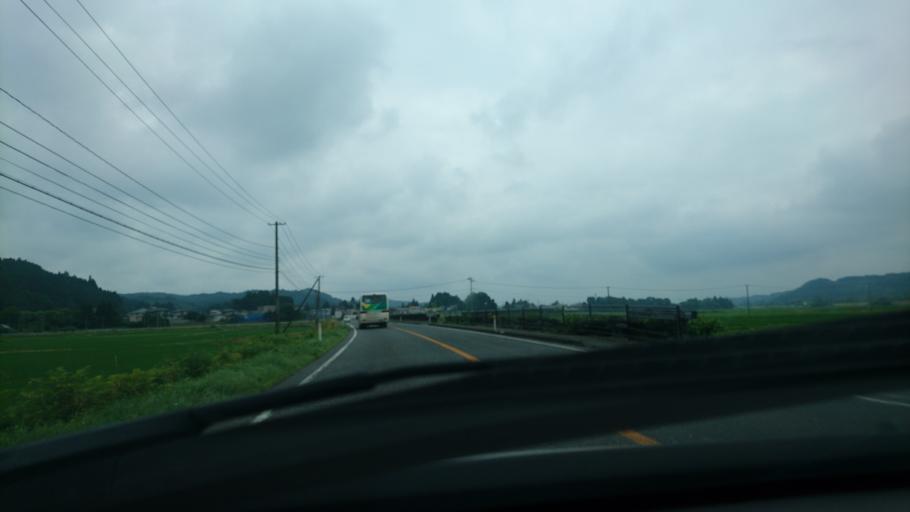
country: JP
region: Miyagi
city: Furukawa
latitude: 38.7148
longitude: 140.8259
